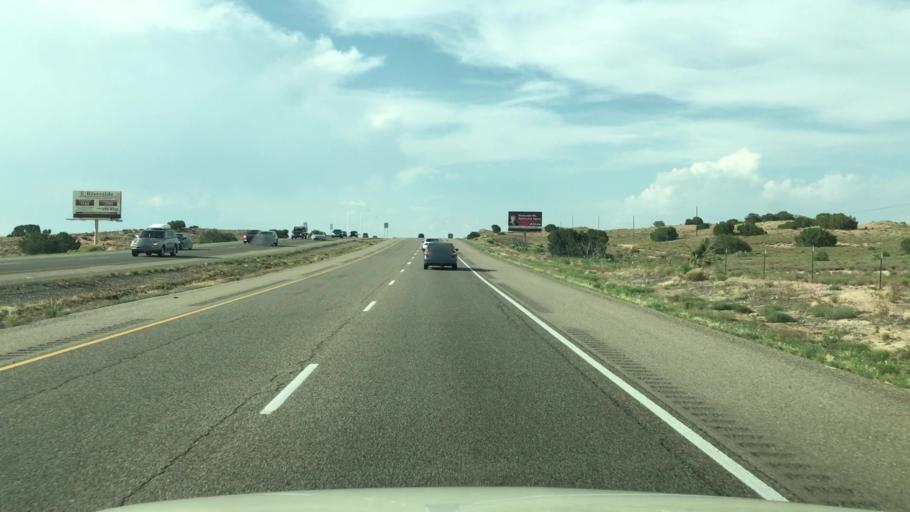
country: US
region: New Mexico
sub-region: Santa Fe County
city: Pojoaque
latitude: 35.9197
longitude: -106.0166
